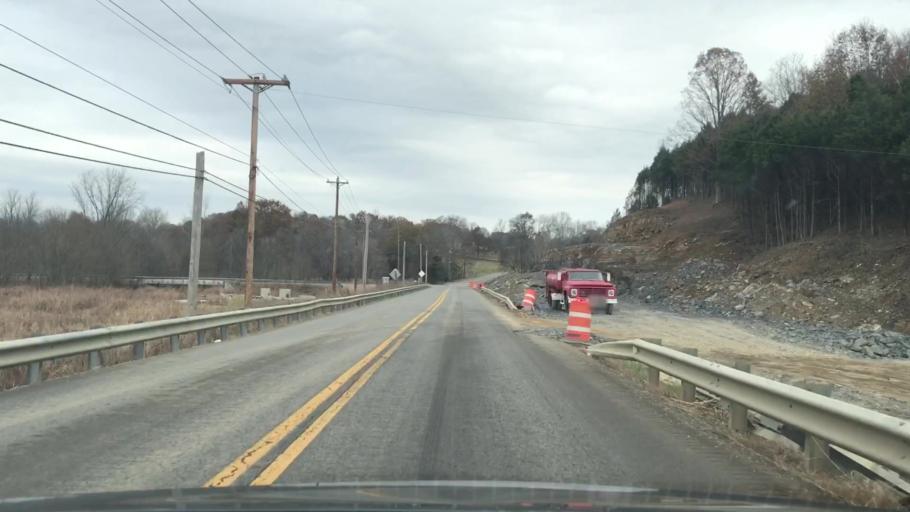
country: US
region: Kentucky
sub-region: Metcalfe County
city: Edmonton
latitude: 36.9312
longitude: -85.6386
